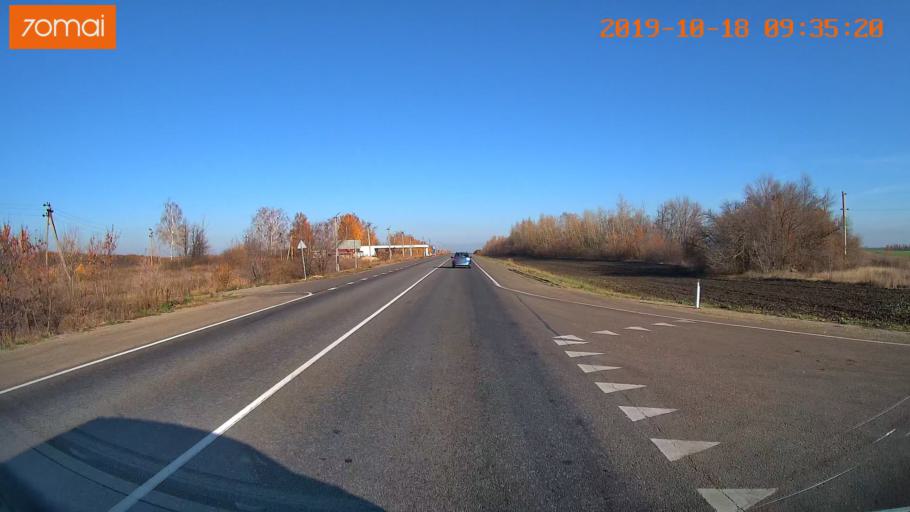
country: RU
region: Tula
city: Yefremov
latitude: 53.1910
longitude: 38.1489
